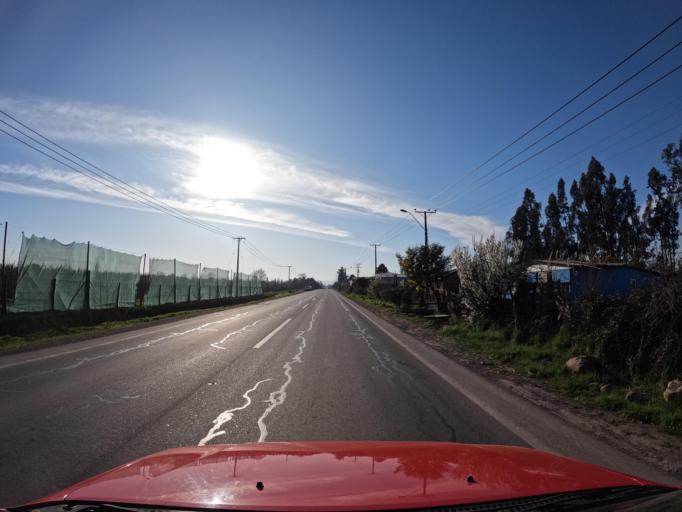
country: CL
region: Maule
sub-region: Provincia de Curico
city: Teno
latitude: -34.8931
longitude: -71.0655
